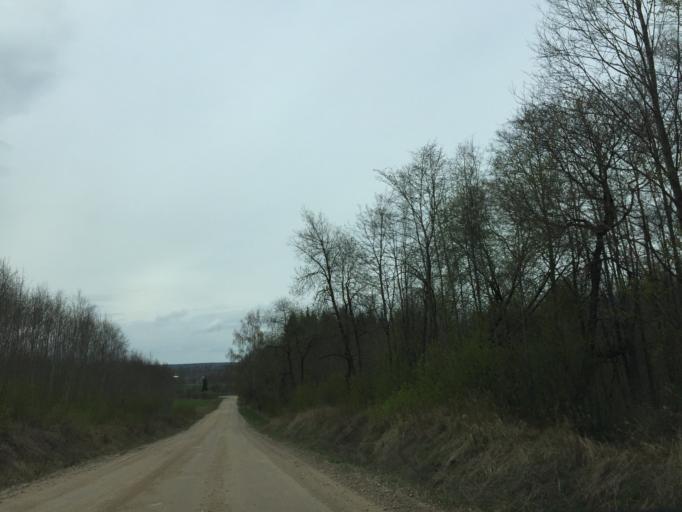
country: LV
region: Priekuli
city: Priekuli
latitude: 57.3436
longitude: 25.3488
